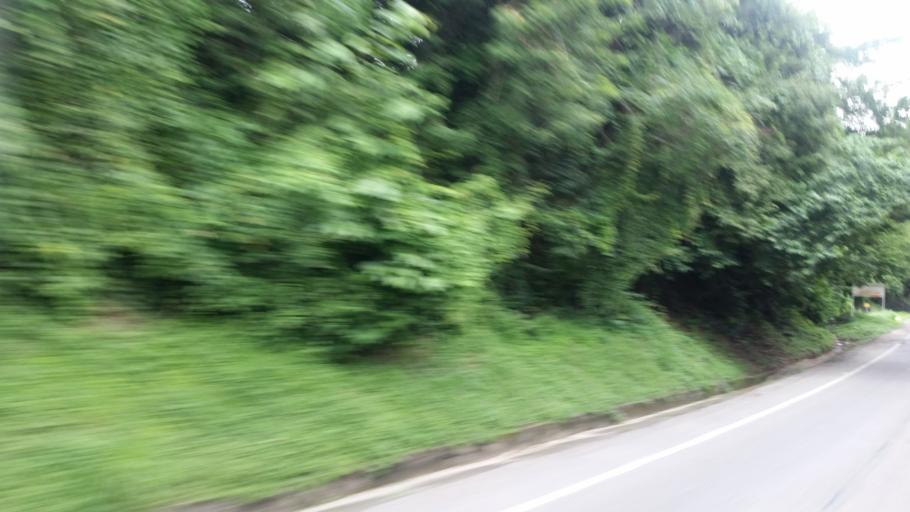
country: CO
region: Magdalena
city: Santa Marta
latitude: 11.2824
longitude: -73.9049
